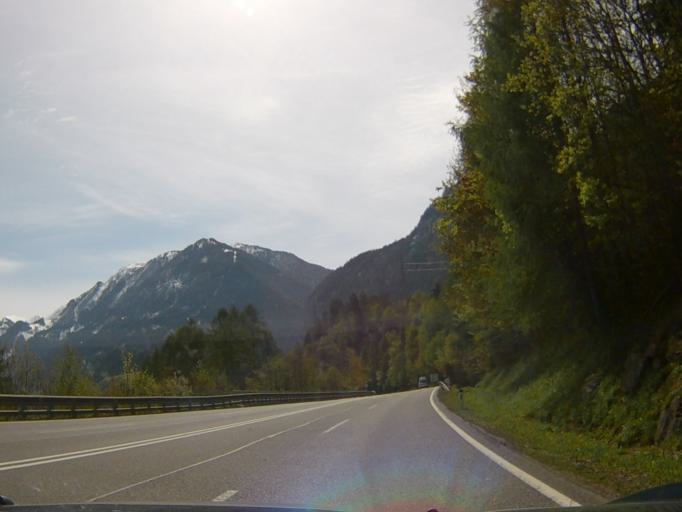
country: AT
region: Salzburg
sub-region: Politischer Bezirk Zell am See
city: Lend
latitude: 47.2995
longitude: 13.0384
